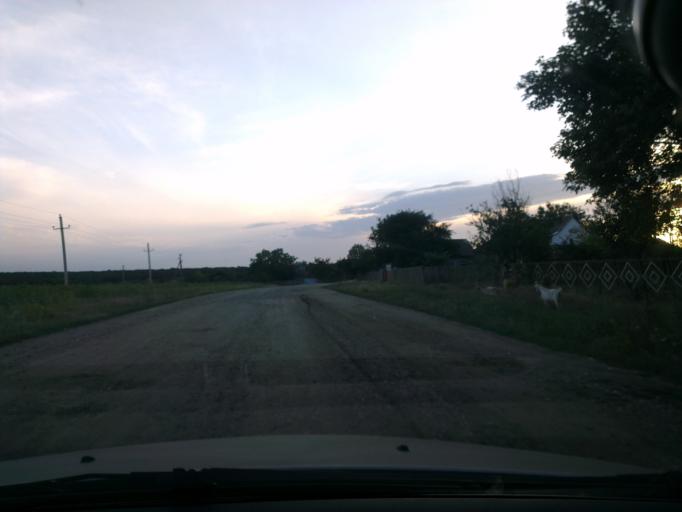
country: MD
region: Cantemir
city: Visniovca
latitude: 46.2858
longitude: 28.3797
